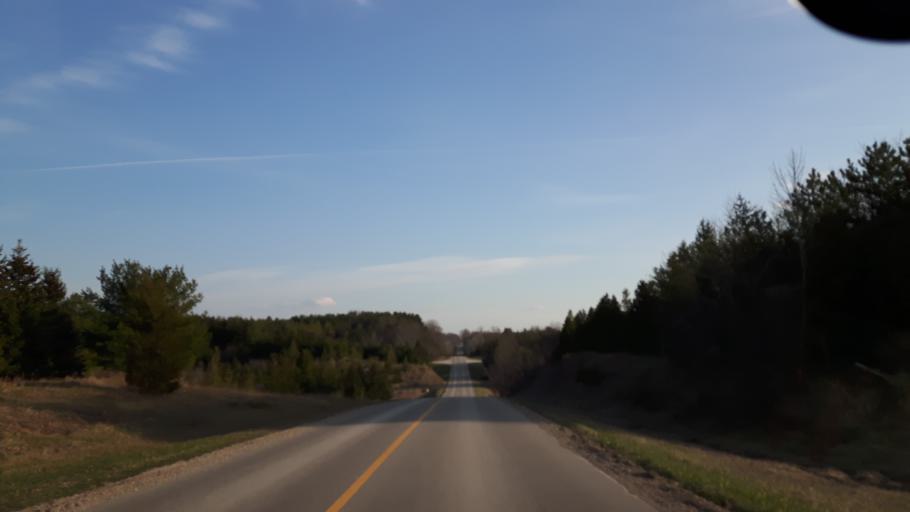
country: CA
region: Ontario
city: Goderich
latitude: 43.6644
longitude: -81.6643
